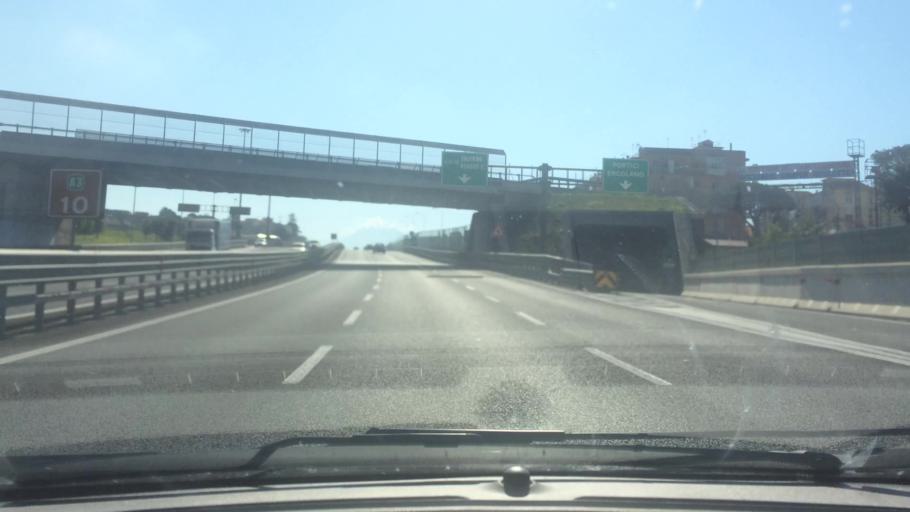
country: IT
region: Campania
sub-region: Provincia di Napoli
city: Ercolano
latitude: 40.8173
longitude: 14.3544
